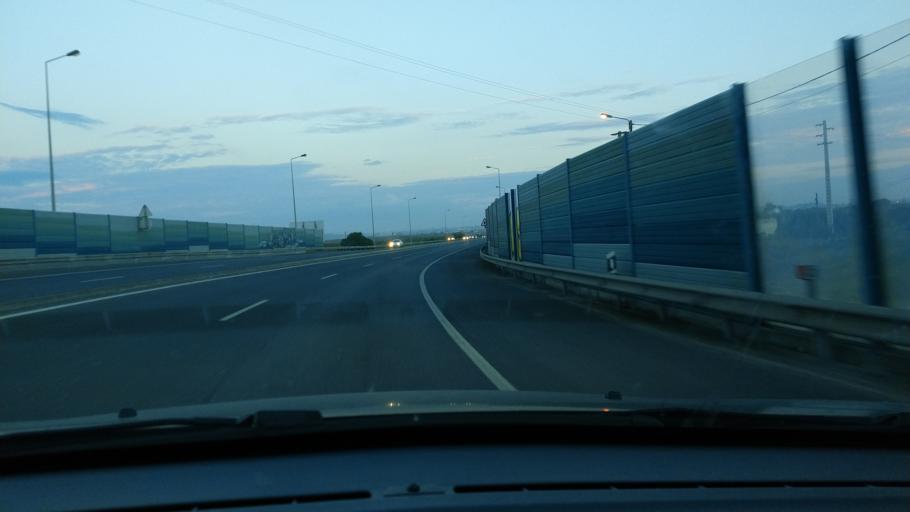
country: PT
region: Leiria
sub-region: Peniche
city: Peniche
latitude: 39.3504
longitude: -9.3566
